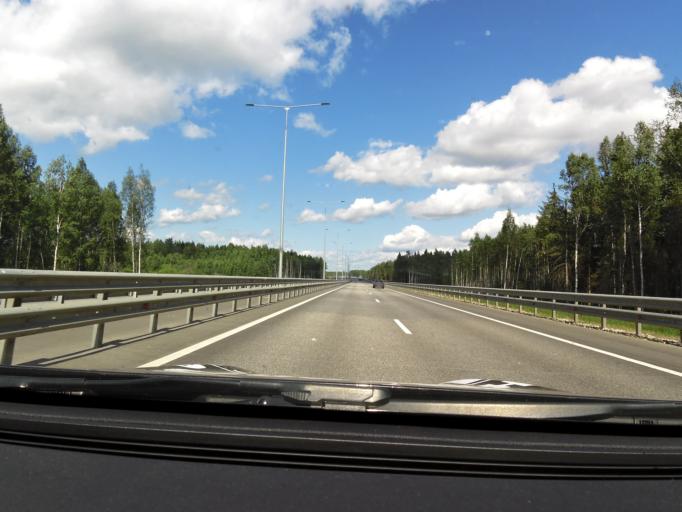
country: RU
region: Tverskaya
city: Vydropuzhsk
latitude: 57.3179
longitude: 34.7547
